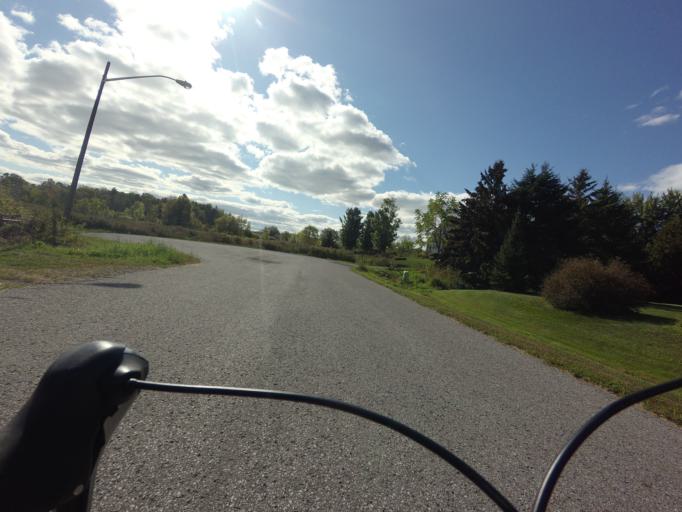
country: CA
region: Ontario
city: Bells Corners
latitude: 45.1524
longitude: -75.6535
